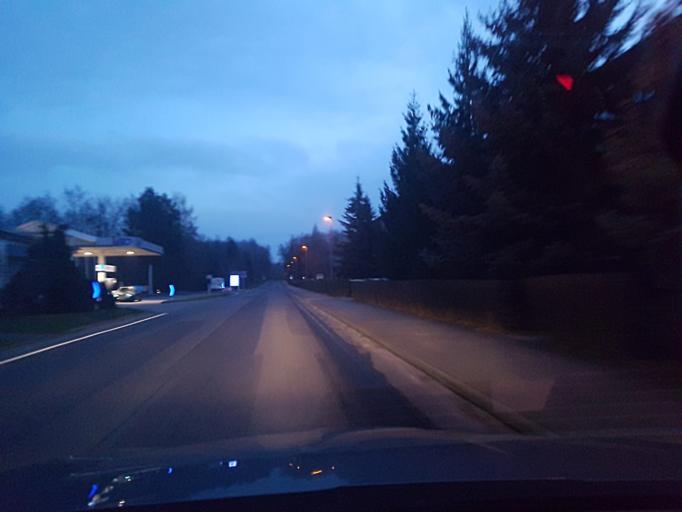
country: DE
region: Brandenburg
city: Trobitz
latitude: 51.5956
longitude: 13.4325
